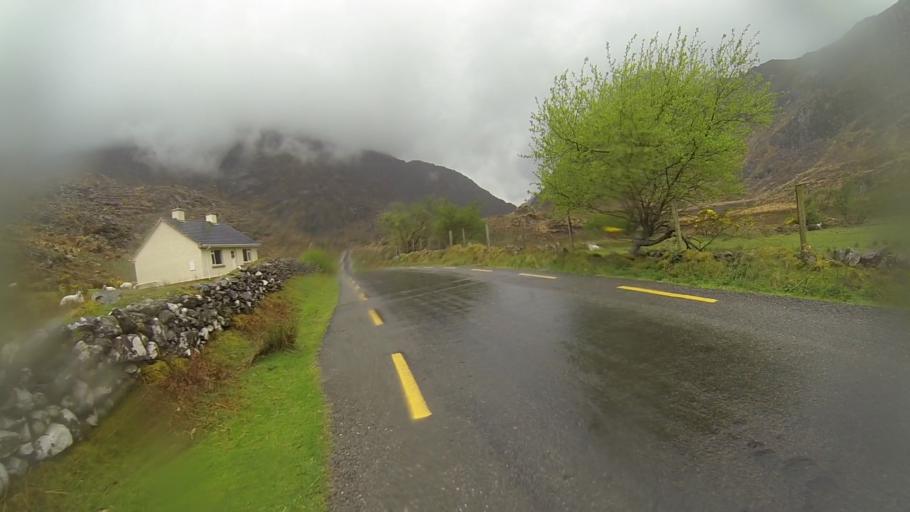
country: IE
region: Munster
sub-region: Ciarrai
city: Cill Airne
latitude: 52.0216
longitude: -9.6367
